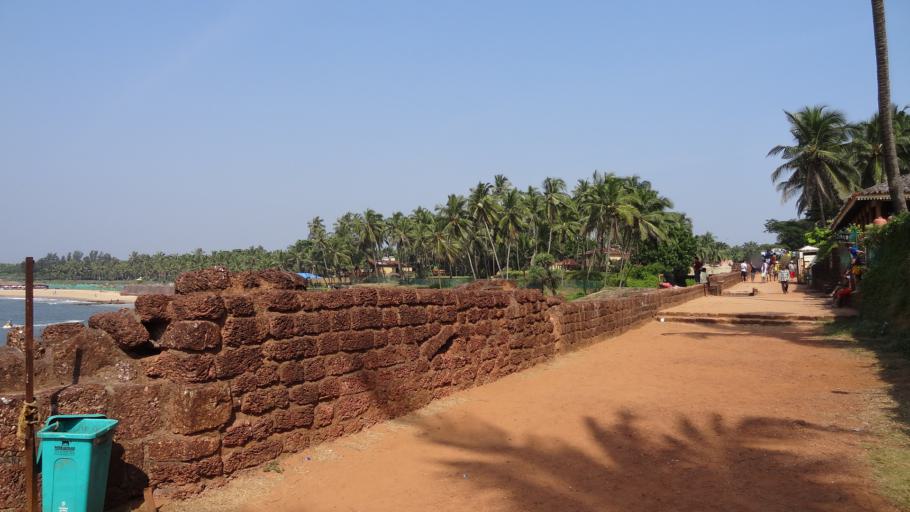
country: IN
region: Goa
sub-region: North Goa
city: Candolim
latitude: 15.4981
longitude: 73.7667
